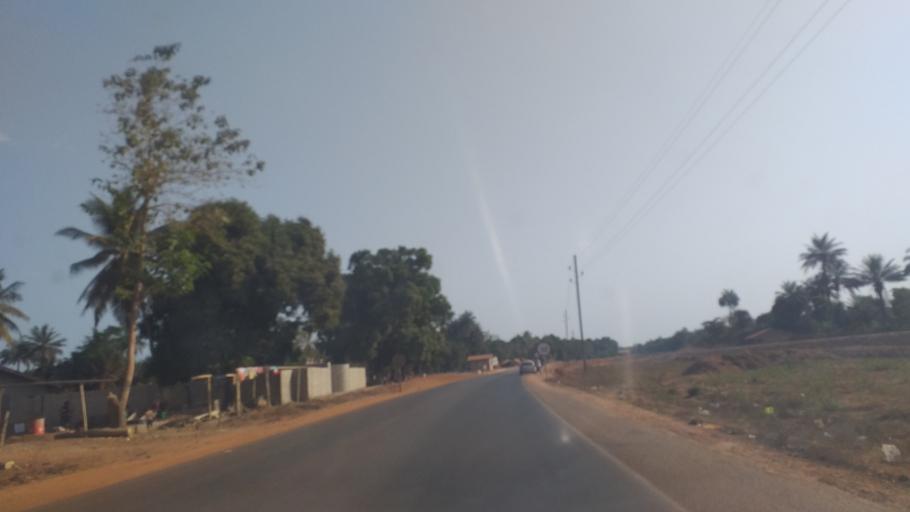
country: GN
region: Boke
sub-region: Boke Prefecture
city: Kamsar
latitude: 10.7367
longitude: -14.5155
